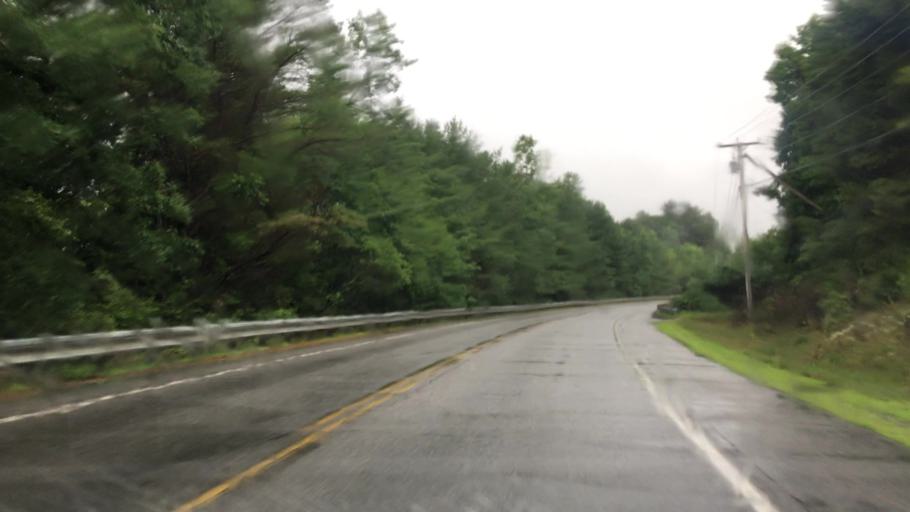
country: US
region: Maine
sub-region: Kennebec County
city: Pittston
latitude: 44.1980
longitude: -69.7613
